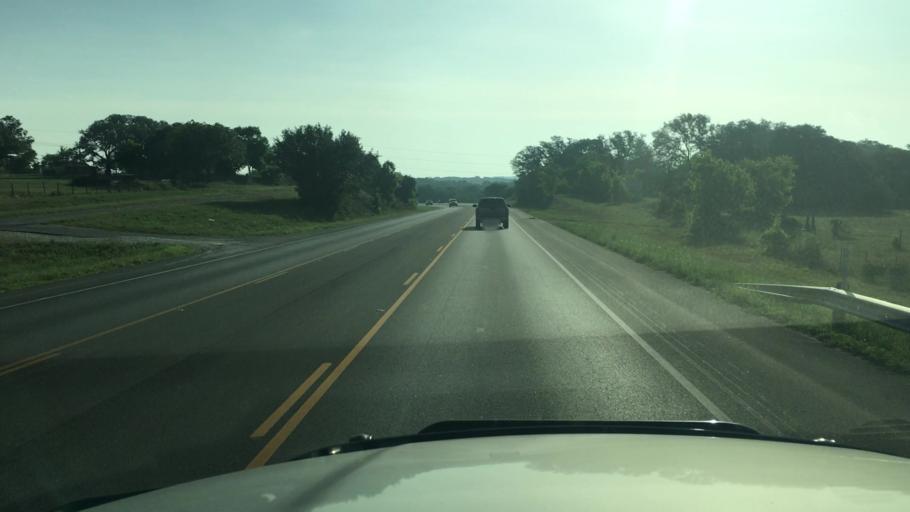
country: US
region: Texas
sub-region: Hays County
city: Dripping Springs
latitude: 30.2004
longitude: -98.1568
